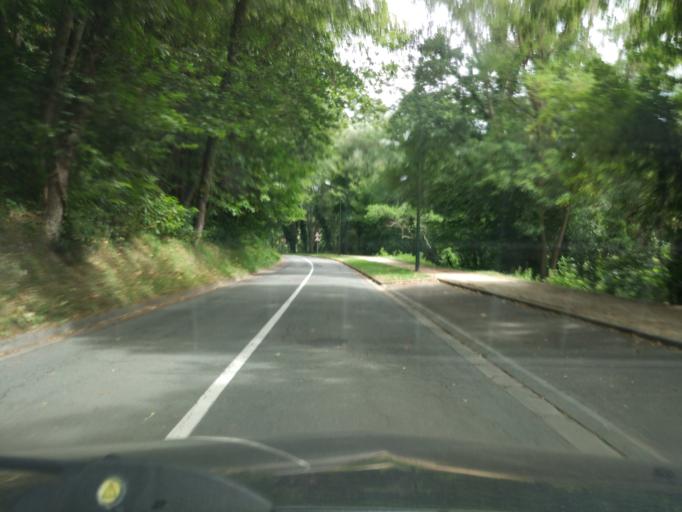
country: FR
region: Ile-de-France
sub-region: Departement de l'Essonne
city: Villiers-le-Bacle
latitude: 48.7197
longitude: 2.1217
